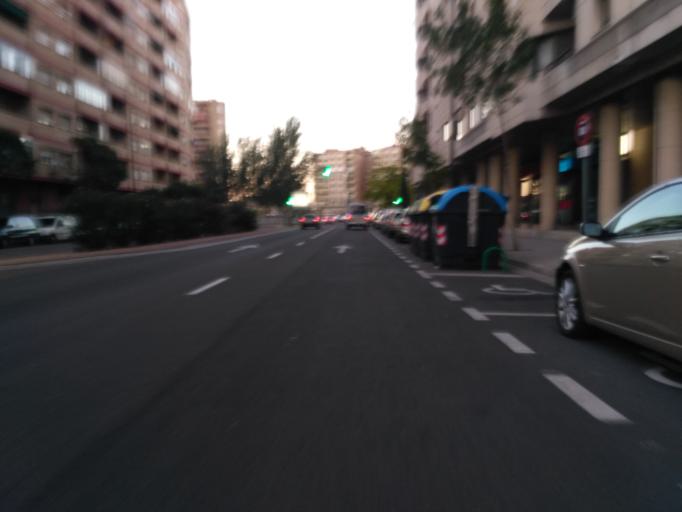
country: ES
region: Aragon
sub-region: Provincia de Zaragoza
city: Almozara
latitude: 41.6528
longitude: -0.8978
